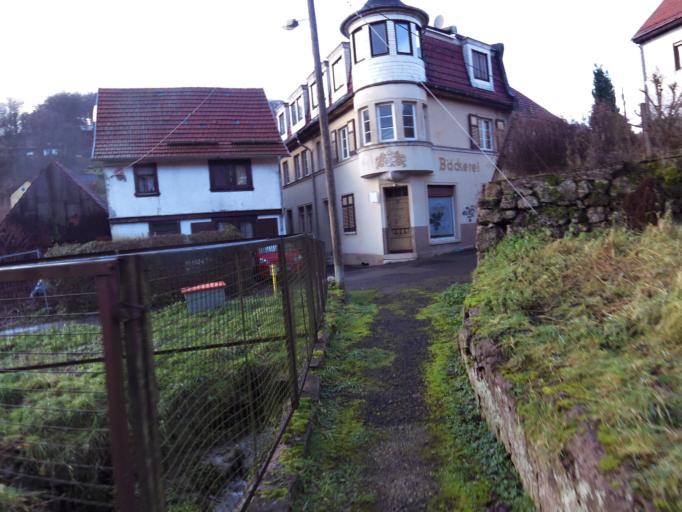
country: DE
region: Thuringia
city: Steinbach
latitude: 50.8336
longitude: 10.3644
